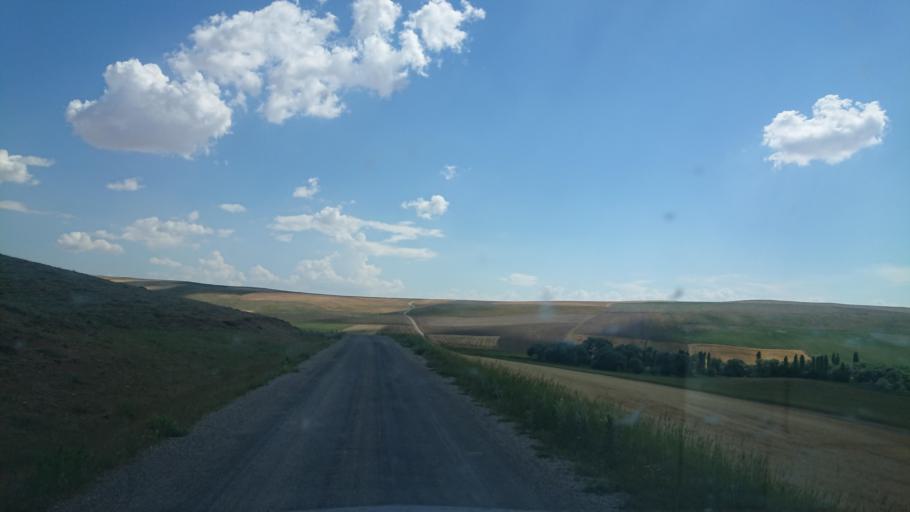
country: TR
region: Aksaray
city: Agacoren
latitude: 38.8246
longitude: 33.7908
